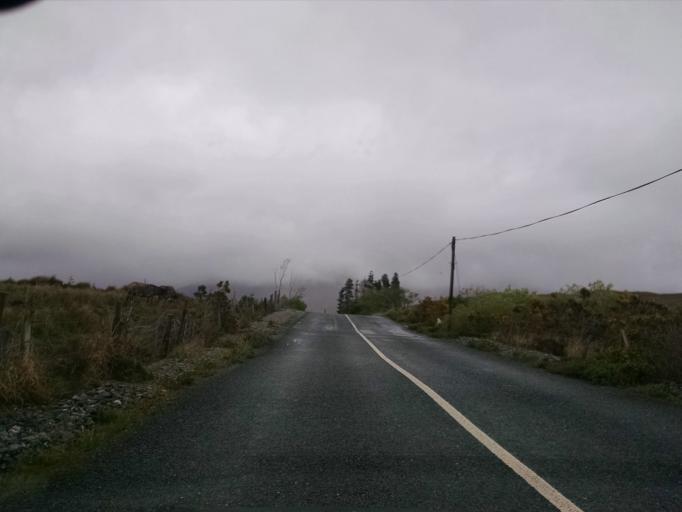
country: IE
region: Connaught
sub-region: County Galway
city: Clifden
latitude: 53.4848
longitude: -9.7402
